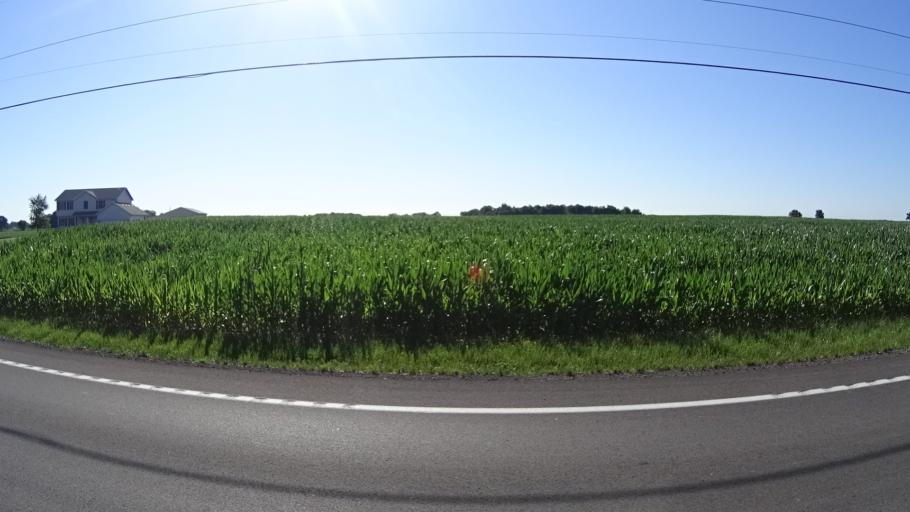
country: US
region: Ohio
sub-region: Erie County
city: Sandusky
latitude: 41.3901
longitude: -82.7355
